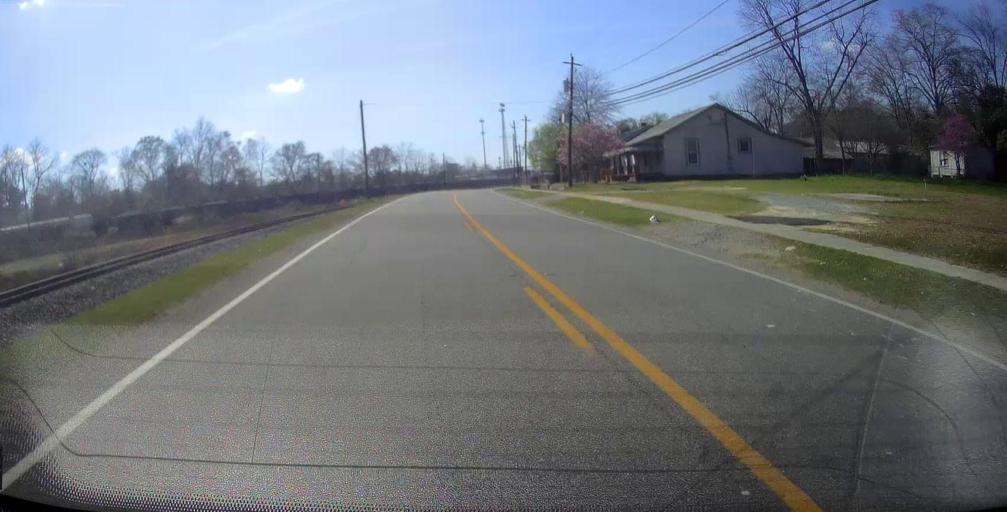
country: US
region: Georgia
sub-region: Wilkinson County
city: Gordon
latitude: 32.8827
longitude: -83.3284
